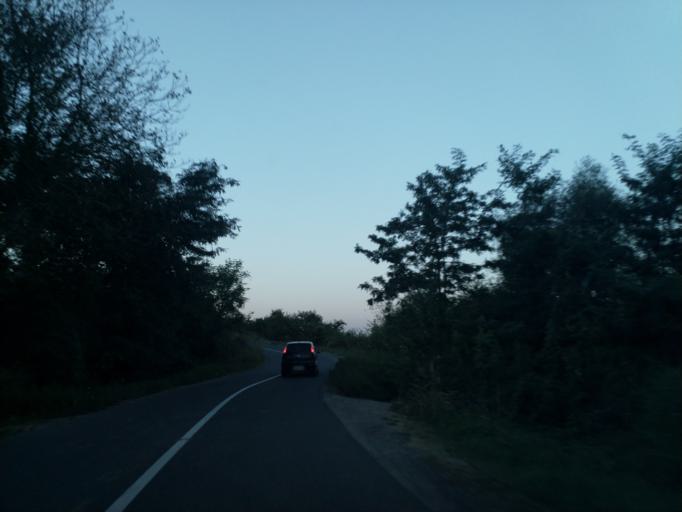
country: RS
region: Central Serbia
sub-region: Rasinski Okrug
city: Krusevac
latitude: 43.6312
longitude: 21.3725
